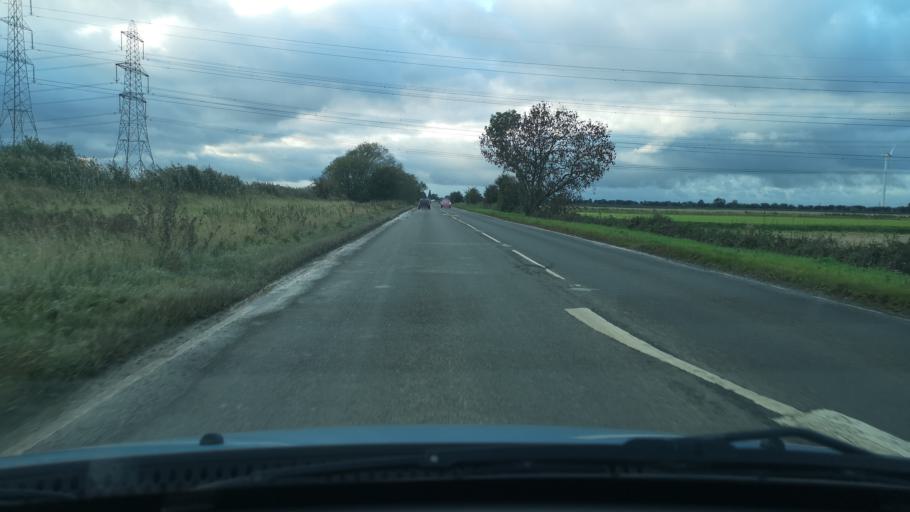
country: GB
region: England
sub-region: North Lincolnshire
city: Gunness
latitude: 53.5770
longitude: -0.7582
